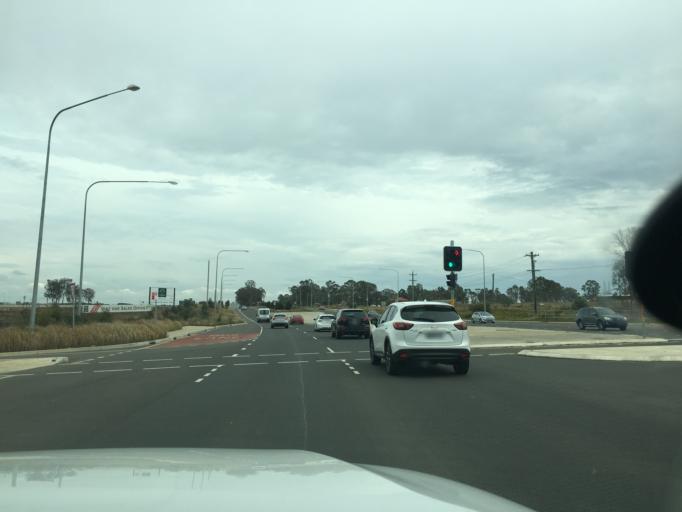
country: AU
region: New South Wales
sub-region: Campbelltown Municipality
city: Denham Court
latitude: -33.9821
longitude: 150.7994
